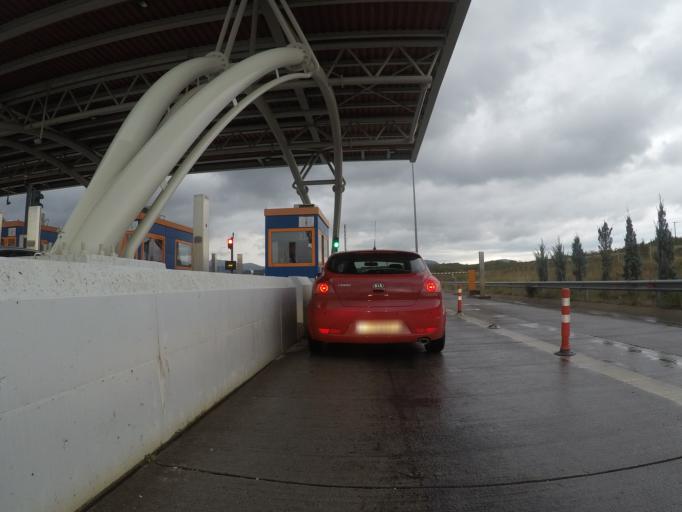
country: GR
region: Peloponnese
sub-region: Nomos Arkadias
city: Megalopoli
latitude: 37.3452
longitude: 22.1103
